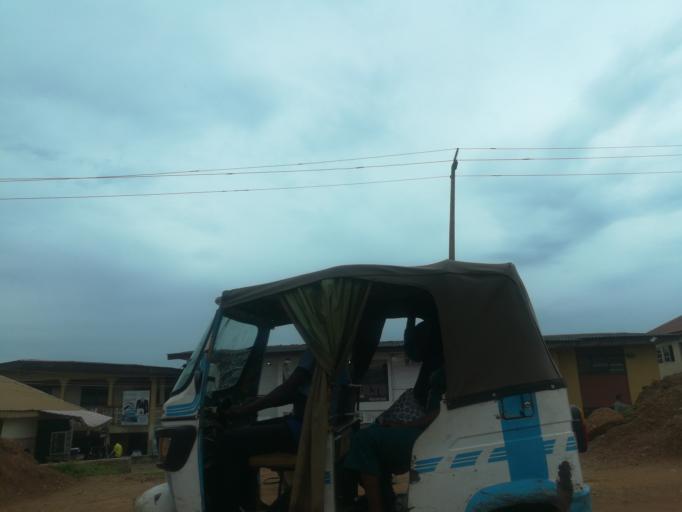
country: NG
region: Oyo
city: Ibadan
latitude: 7.3899
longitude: 3.9516
